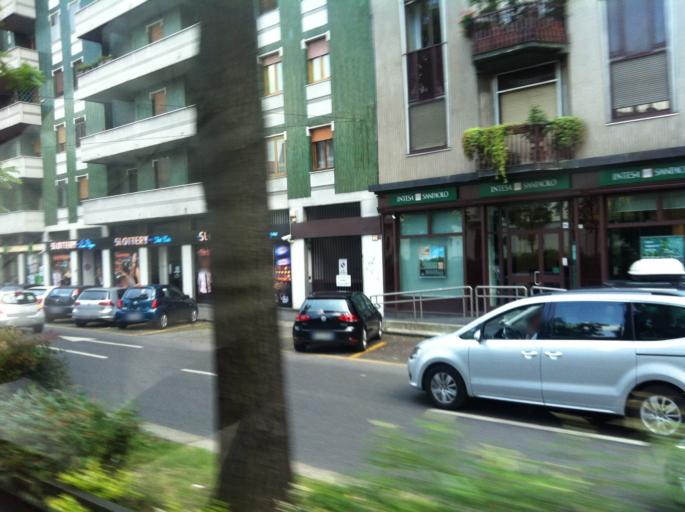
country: IT
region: Lombardy
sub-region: Citta metropolitana di Milano
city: Milano
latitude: 45.4818
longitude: 9.2206
